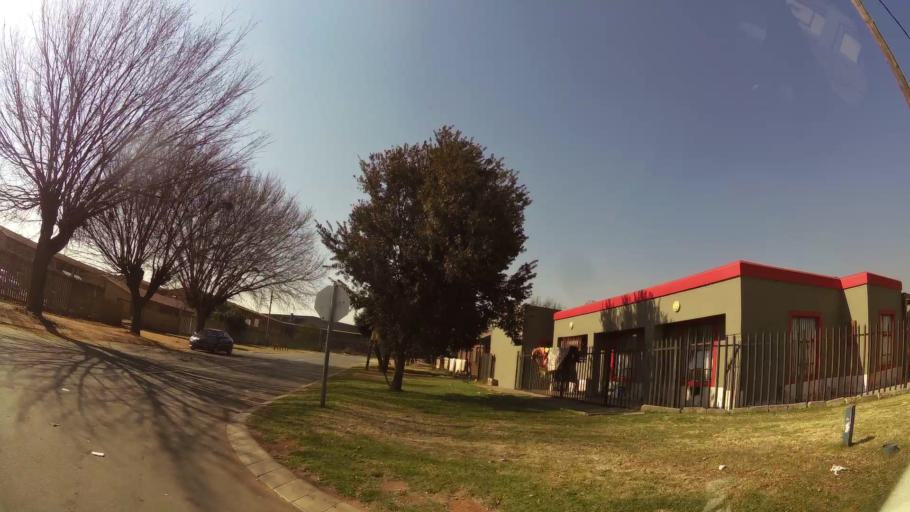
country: ZA
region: Gauteng
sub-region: Ekurhuleni Metropolitan Municipality
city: Boksburg
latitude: -26.2136
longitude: 28.2908
